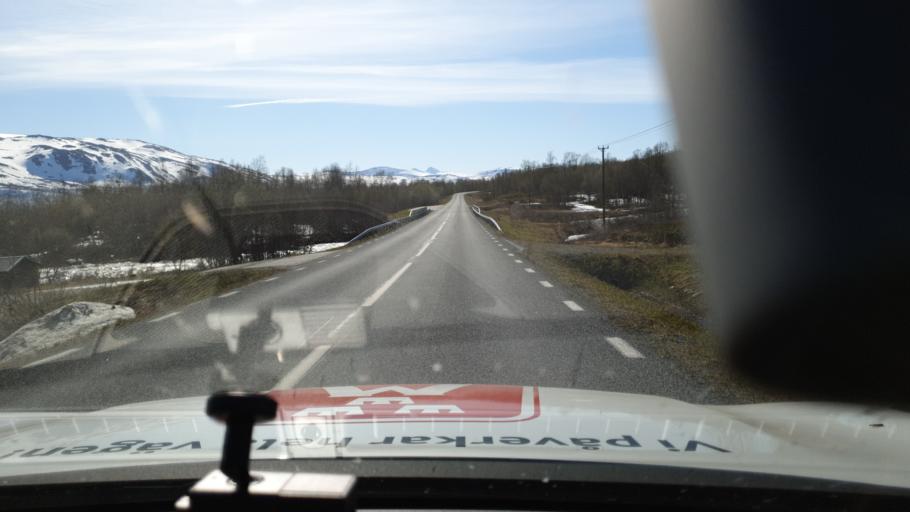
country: NO
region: Nordland
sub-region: Rana
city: Mo i Rana
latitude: 66.0375
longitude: 15.0564
